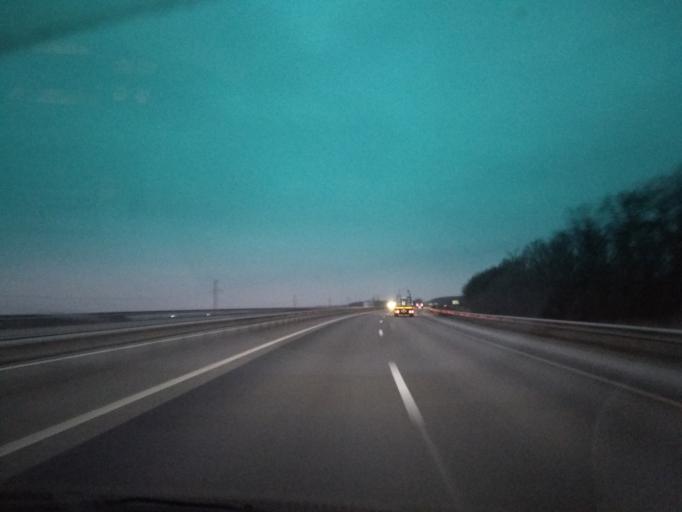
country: RU
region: Krasnodarskiy
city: Saratovskaya
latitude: 44.7839
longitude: 39.2359
